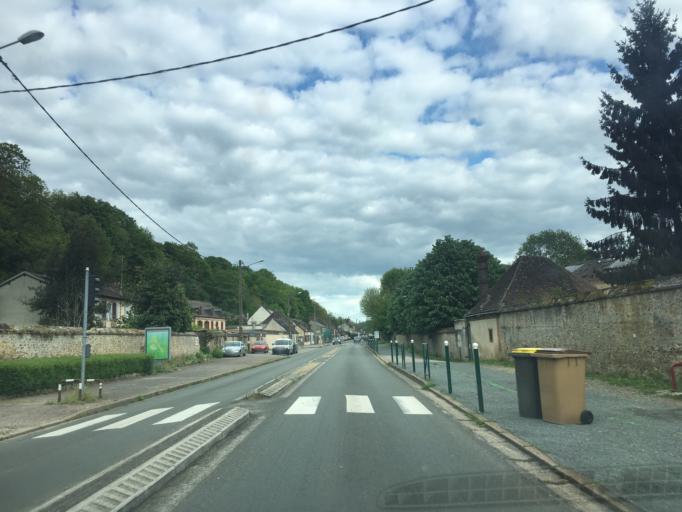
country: FR
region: Haute-Normandie
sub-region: Departement de l'Eure
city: La Madeleine-de-Nonancourt
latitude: 48.7678
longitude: 1.2060
